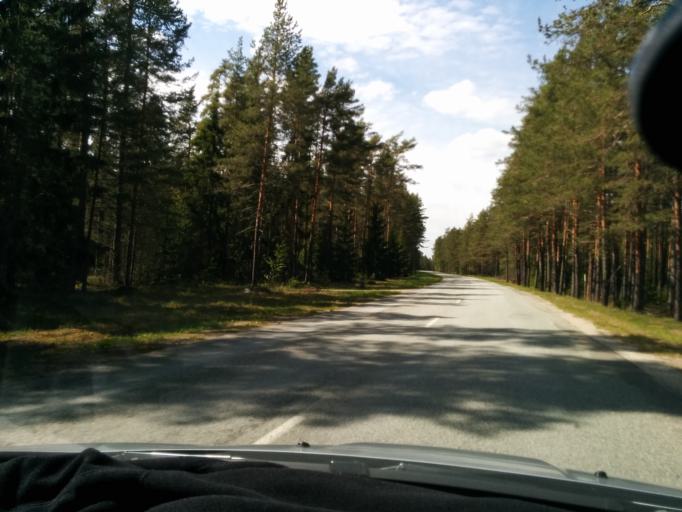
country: EE
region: Laeaene-Virumaa
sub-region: Kadrina vald
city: Kadrina
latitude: 59.5532
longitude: 26.0086
